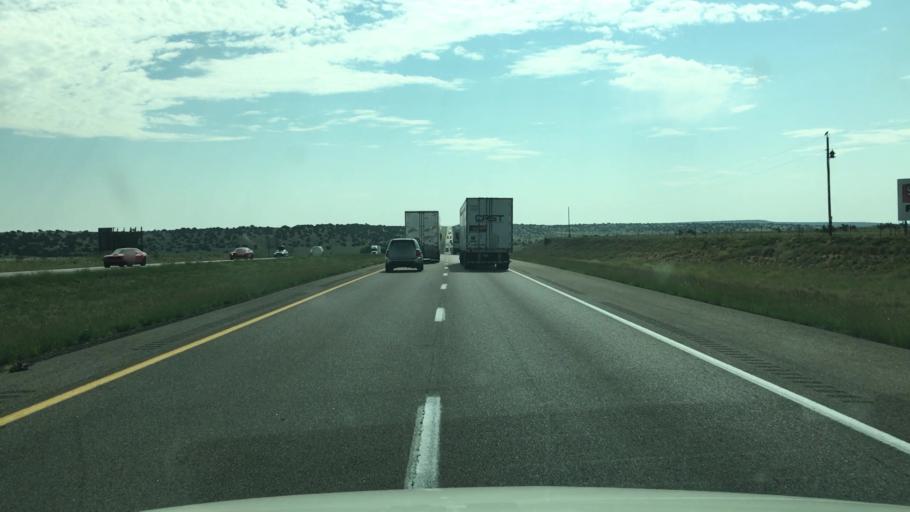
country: US
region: New Mexico
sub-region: Guadalupe County
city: Santa Rosa
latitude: 34.9758
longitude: -104.9806
